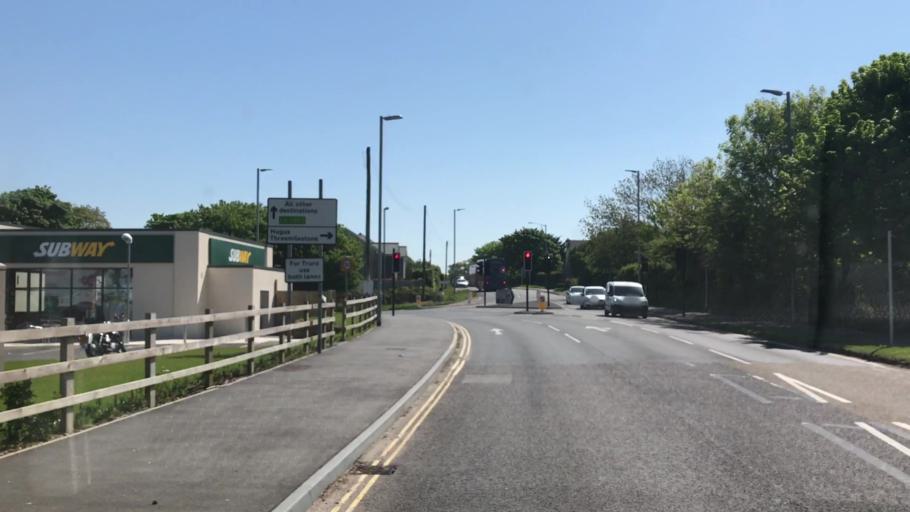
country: GB
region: England
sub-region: Cornwall
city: Chacewater
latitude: 50.2635
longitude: -5.1202
